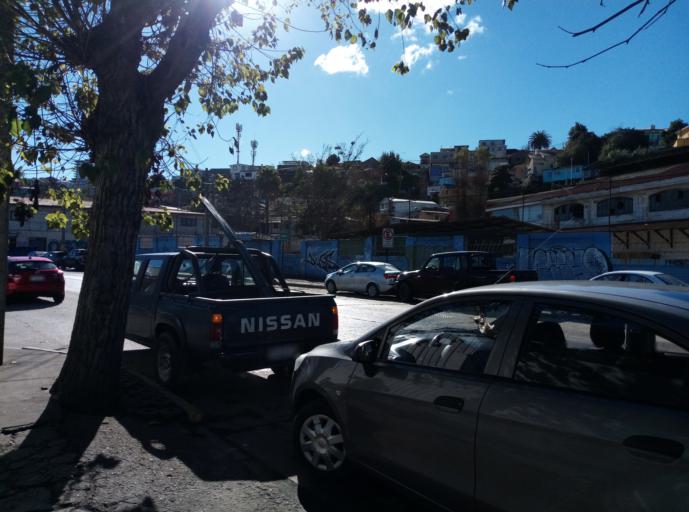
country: CL
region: Valparaiso
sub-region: Provincia de Valparaiso
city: Vina del Mar
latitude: -33.0098
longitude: -71.5416
